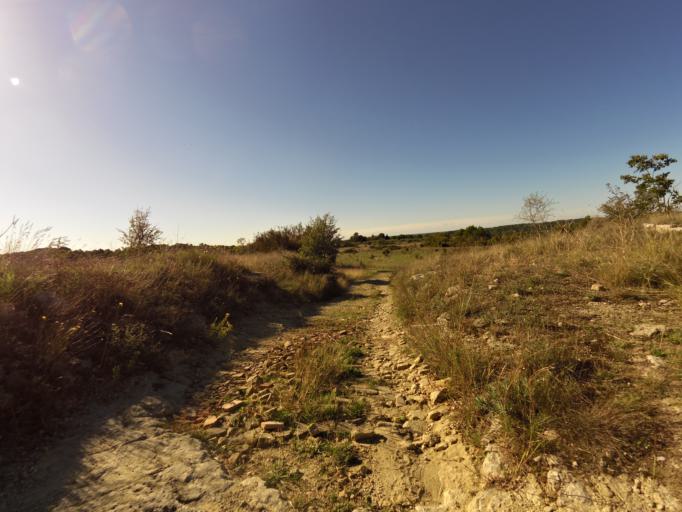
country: FR
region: Languedoc-Roussillon
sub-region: Departement du Gard
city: Aigues-Vives
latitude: 43.7336
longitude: 4.1668
